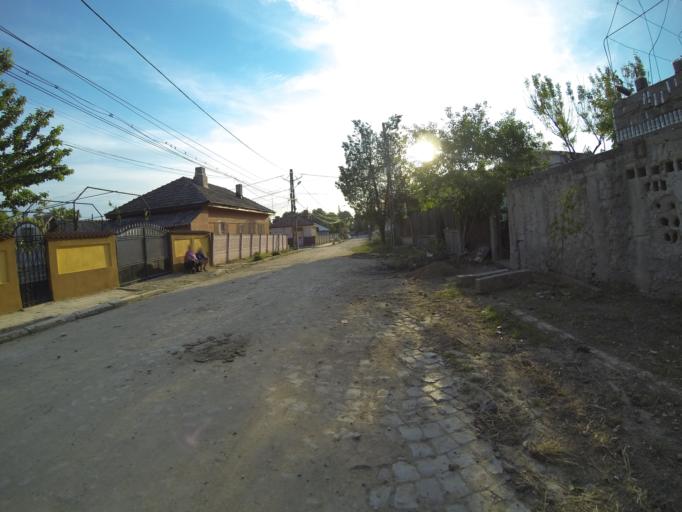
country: RO
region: Dolj
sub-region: Comuna Segarcea
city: Segarcea
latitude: 44.0970
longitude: 23.7469
